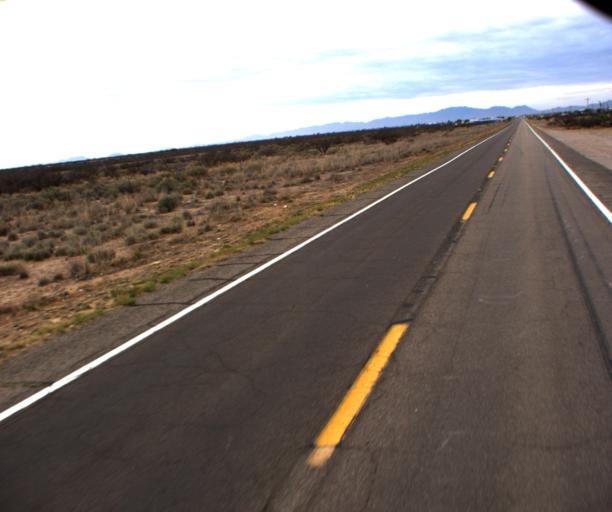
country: US
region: Arizona
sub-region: Cochise County
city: Willcox
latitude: 32.2881
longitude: -109.8079
